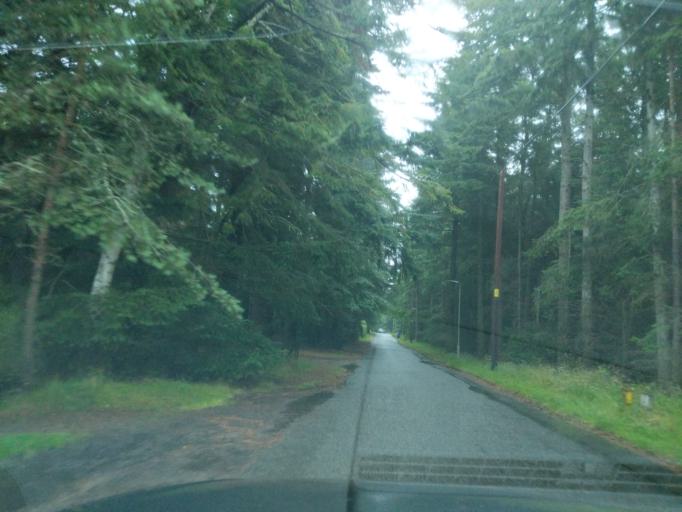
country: GB
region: Scotland
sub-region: Aberdeenshire
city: Aboyne
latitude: 57.0710
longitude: -2.8020
